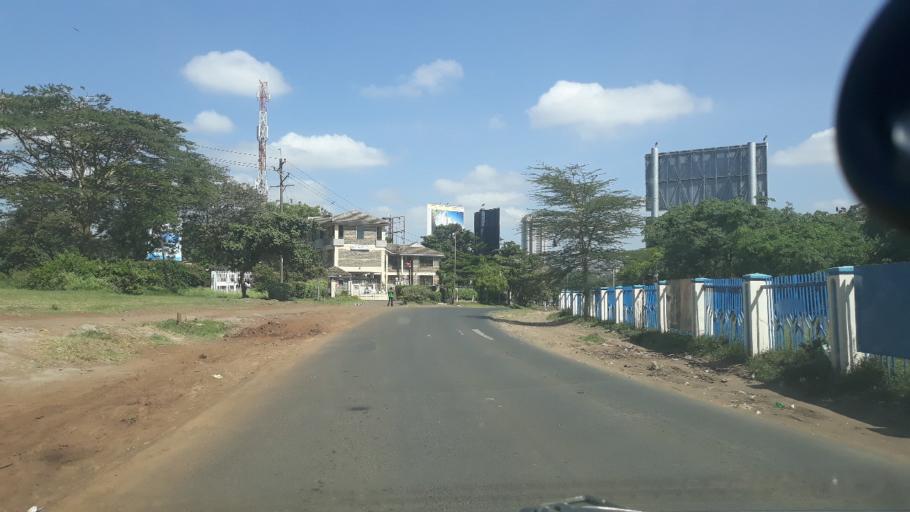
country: KE
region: Nairobi Area
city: Nairobi
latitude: -1.3014
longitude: 36.8239
